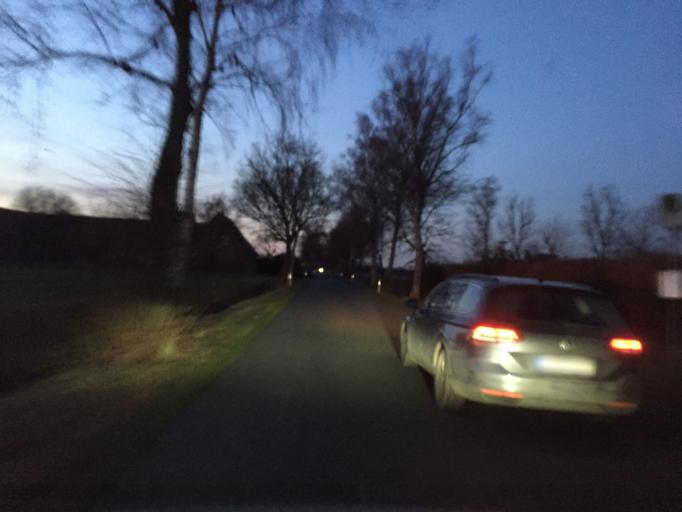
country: DE
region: Lower Saxony
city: Kirchdorf
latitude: 52.6366
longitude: 8.8440
